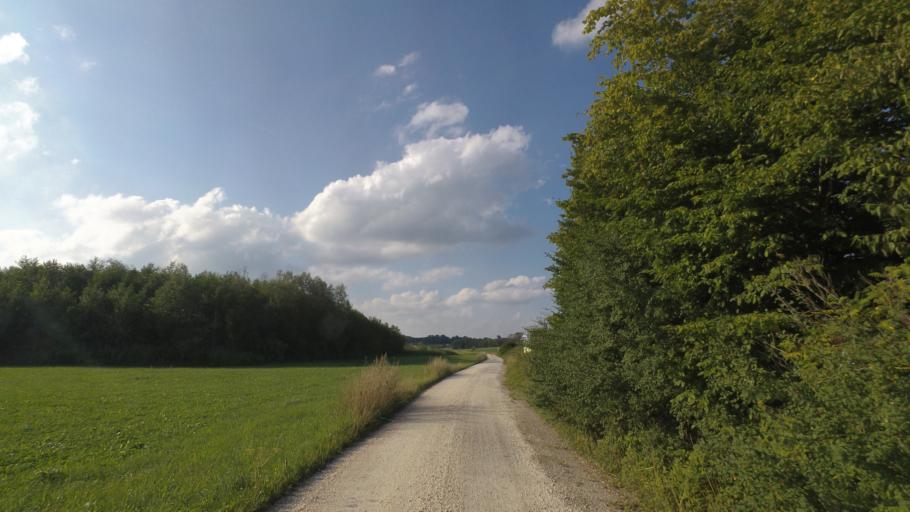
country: DE
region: Bavaria
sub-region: Upper Bavaria
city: Chieming
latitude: 47.9007
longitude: 12.5648
